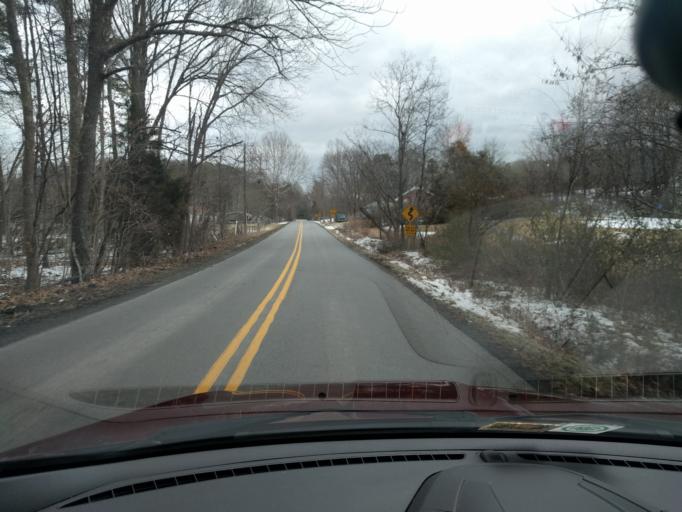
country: US
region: Virginia
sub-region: Alleghany County
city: Clifton Forge
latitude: 37.8253
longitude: -79.7893
